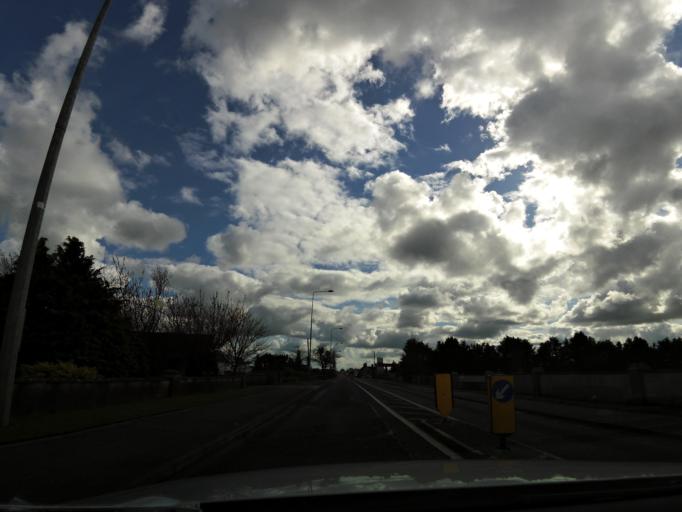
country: IE
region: Leinster
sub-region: Laois
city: Rathdowney
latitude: 52.7539
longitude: -7.5527
